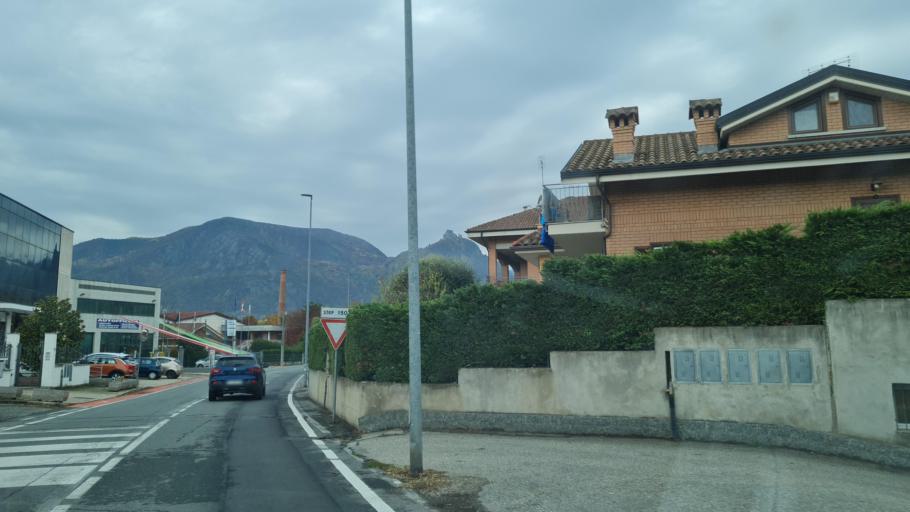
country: IT
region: Piedmont
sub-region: Provincia di Torino
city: Villar Dora
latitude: 45.1114
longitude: 7.3849
